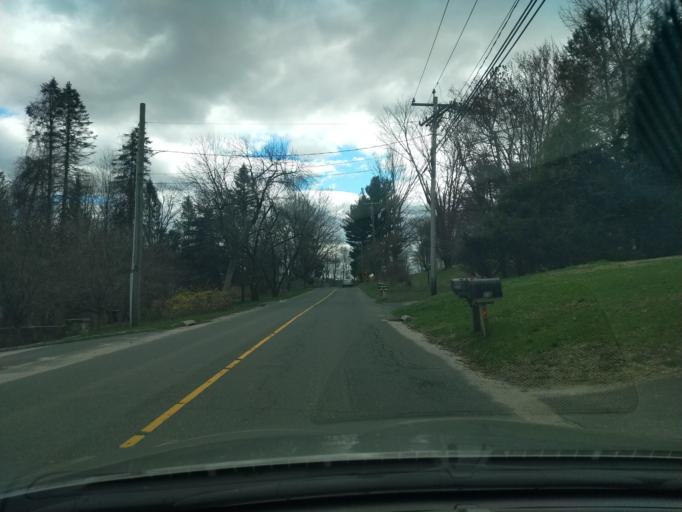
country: US
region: Connecticut
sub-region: Fairfield County
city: Bethel
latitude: 41.3862
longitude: -73.3731
